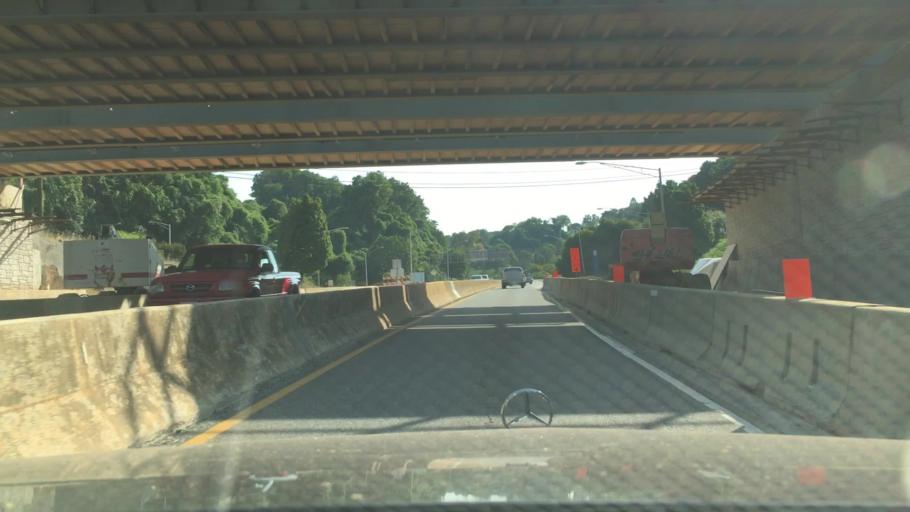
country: US
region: Virginia
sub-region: City of Lynchburg
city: Lynchburg
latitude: 37.4086
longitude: -79.1364
